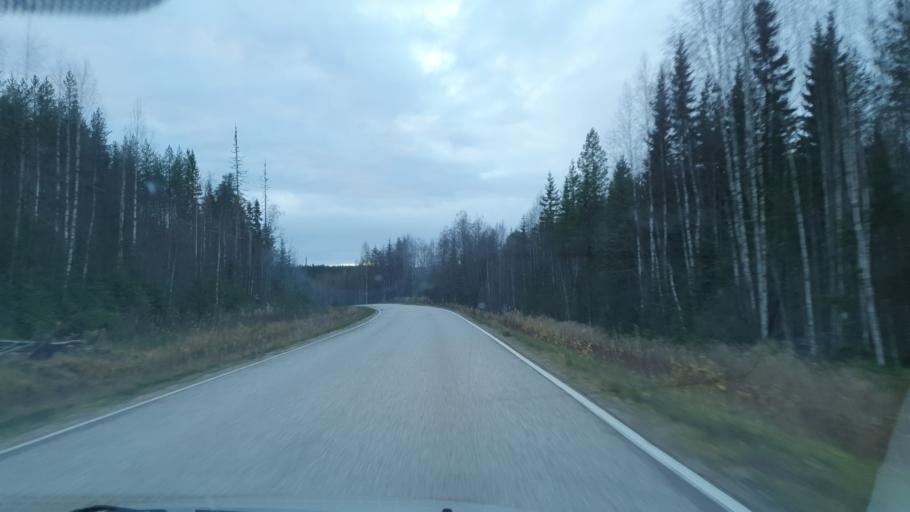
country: FI
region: Kainuu
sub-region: Kajaani
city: Ristijaervi
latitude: 64.4270
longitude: 28.3899
